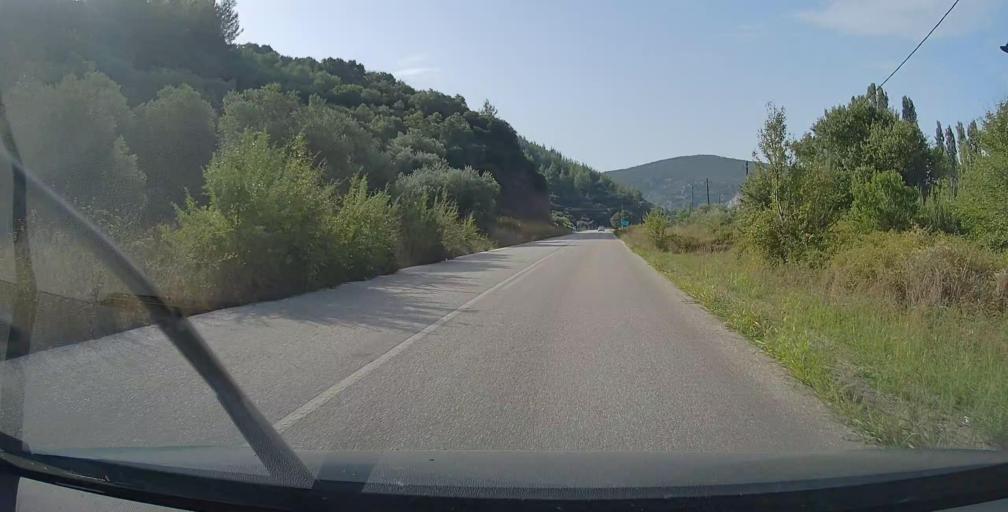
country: GR
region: Central Macedonia
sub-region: Nomos Chalkidikis
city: Sykia
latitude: 39.9694
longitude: 23.9270
